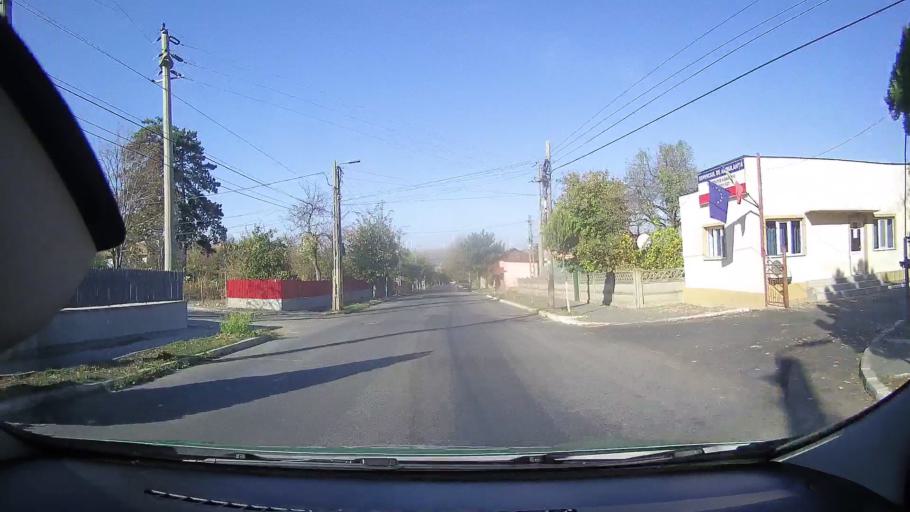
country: RO
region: Tulcea
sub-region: Oras Babadag
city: Babadag
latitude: 44.8891
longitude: 28.7302
